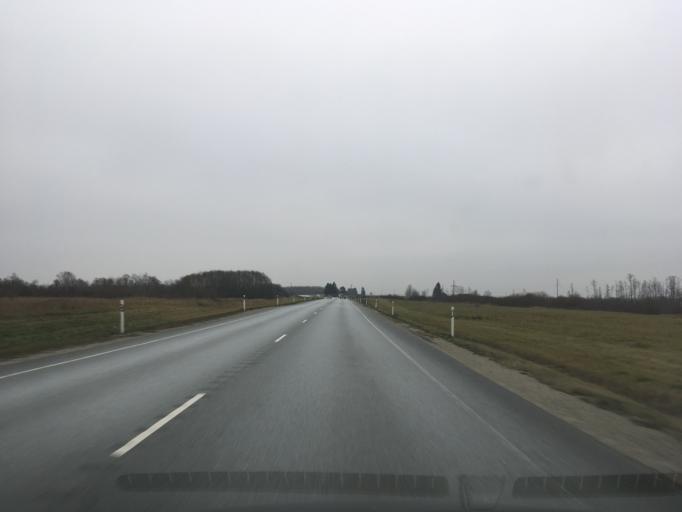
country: EE
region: Ida-Virumaa
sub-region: Kivioli linn
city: Kivioli
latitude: 59.4252
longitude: 26.9617
